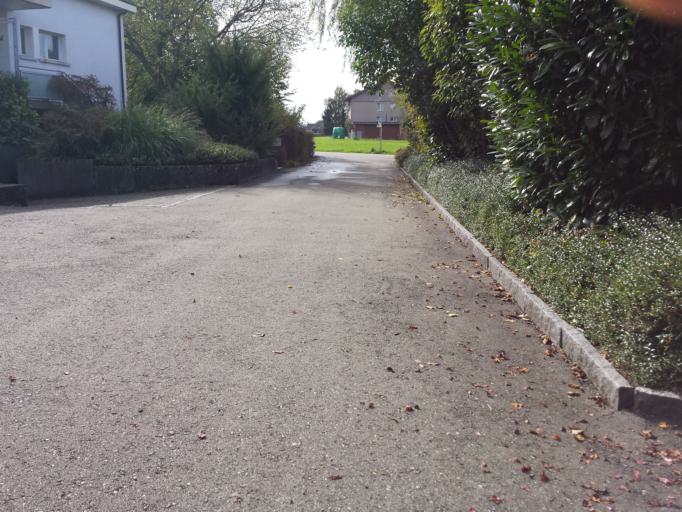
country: CH
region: Thurgau
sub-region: Arbon District
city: Salmsach
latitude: 47.5667
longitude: 9.3601
